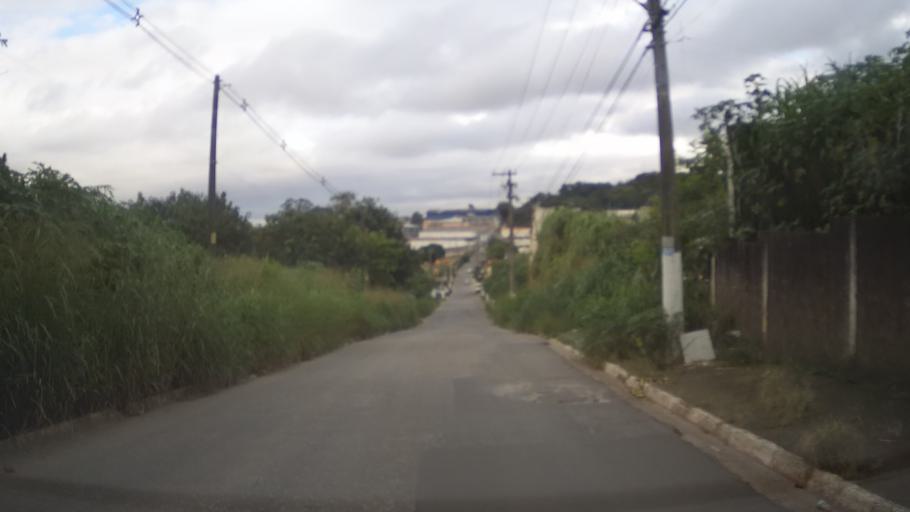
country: BR
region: Sao Paulo
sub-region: Itaquaquecetuba
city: Itaquaquecetuba
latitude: -23.4551
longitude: -46.3939
